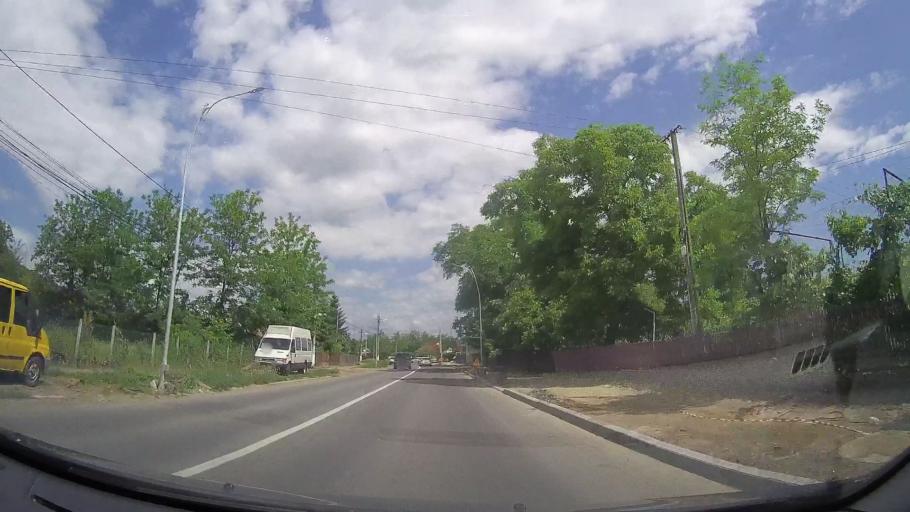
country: RO
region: Prahova
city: Drajna de Jos
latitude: 45.2041
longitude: 26.0430
